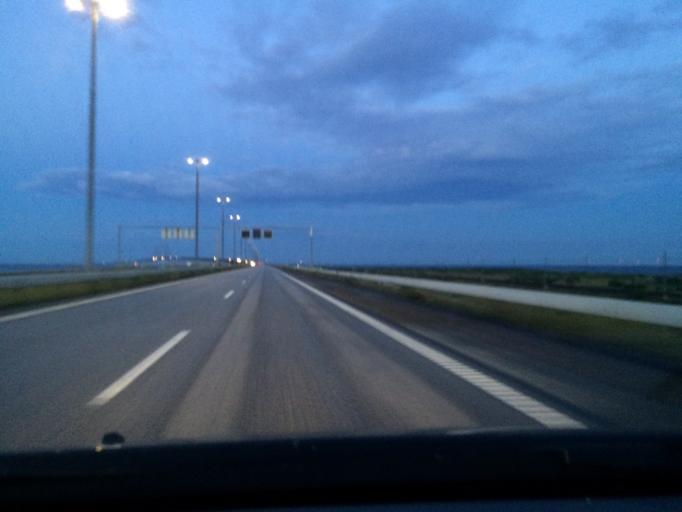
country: DK
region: Capital Region
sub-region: Dragor Kommune
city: Dragor
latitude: 55.5998
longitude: 12.7518
